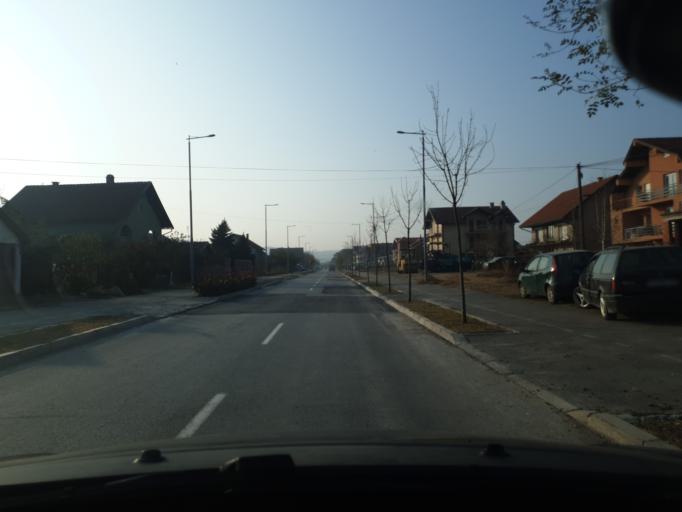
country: RS
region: Central Serbia
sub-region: Jablanicki Okrug
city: Leskovac
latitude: 43.0013
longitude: 21.9238
